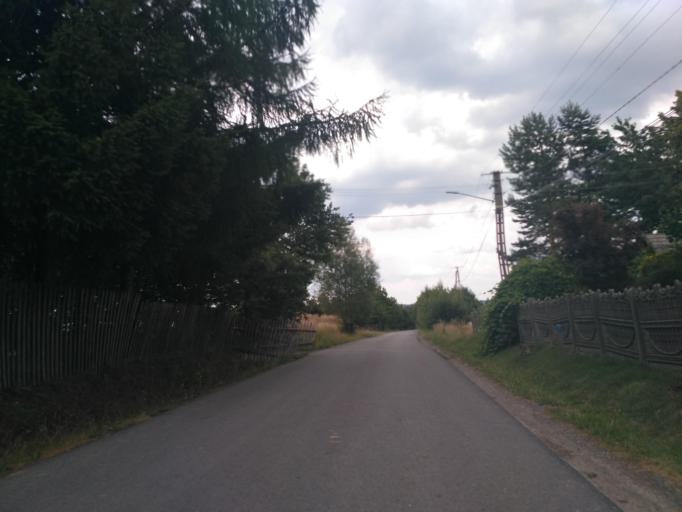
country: PL
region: Subcarpathian Voivodeship
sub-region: Powiat ropczycko-sedziszowski
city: Niedzwiada
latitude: 50.0292
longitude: 21.5188
